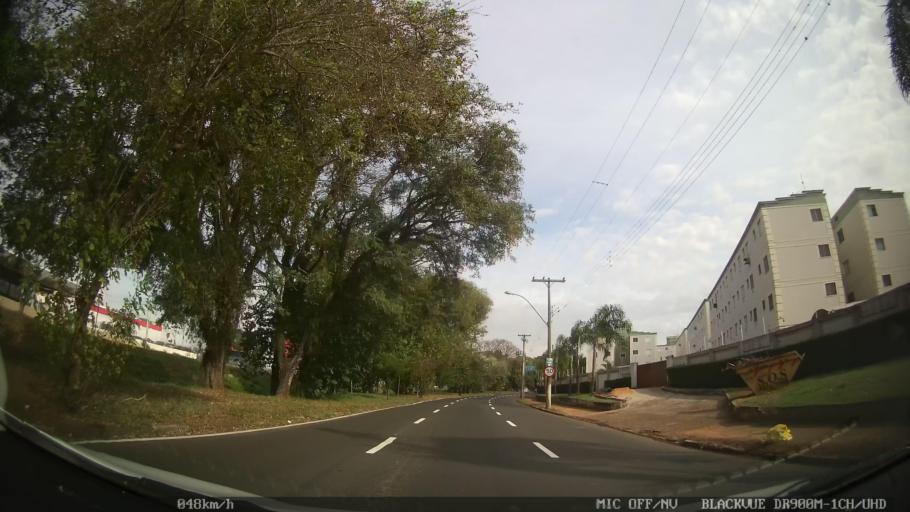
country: BR
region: Sao Paulo
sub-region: Piracicaba
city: Piracicaba
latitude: -22.7366
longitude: -47.6296
